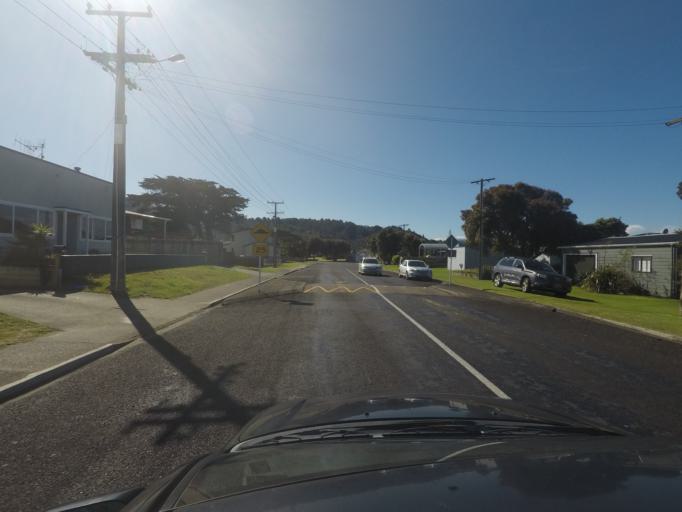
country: NZ
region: Bay of Plenty
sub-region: Western Bay of Plenty District
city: Waihi Beach
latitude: -37.4036
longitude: 175.9405
